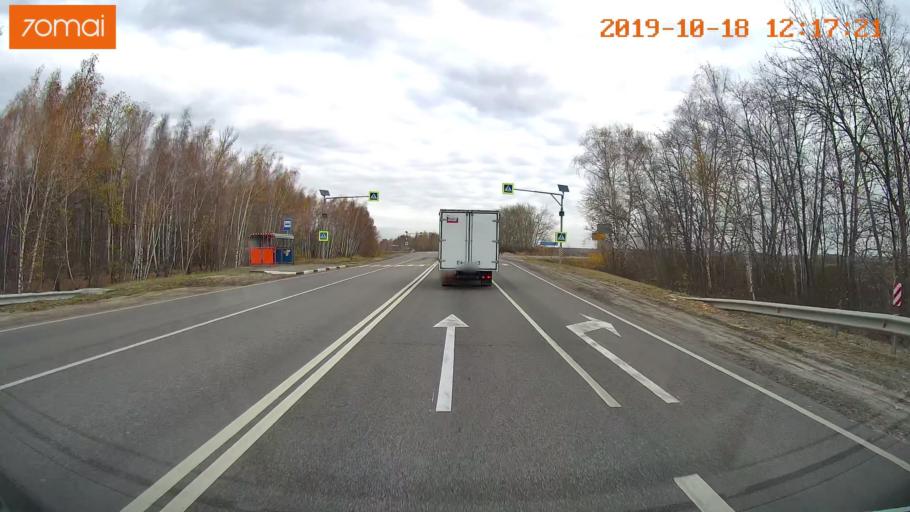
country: RU
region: Rjazan
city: Zakharovo
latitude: 54.4569
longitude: 39.4425
